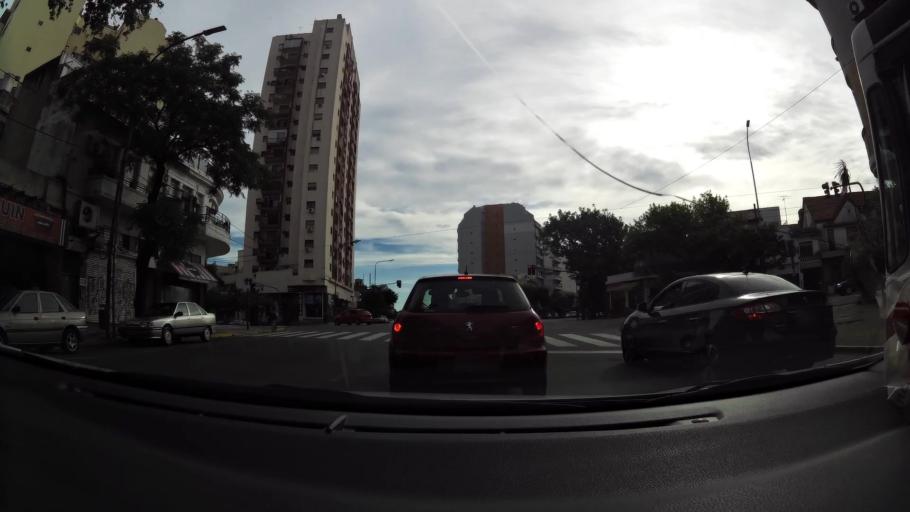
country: AR
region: Buenos Aires F.D.
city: Villa Santa Rita
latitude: -34.6339
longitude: -58.4325
